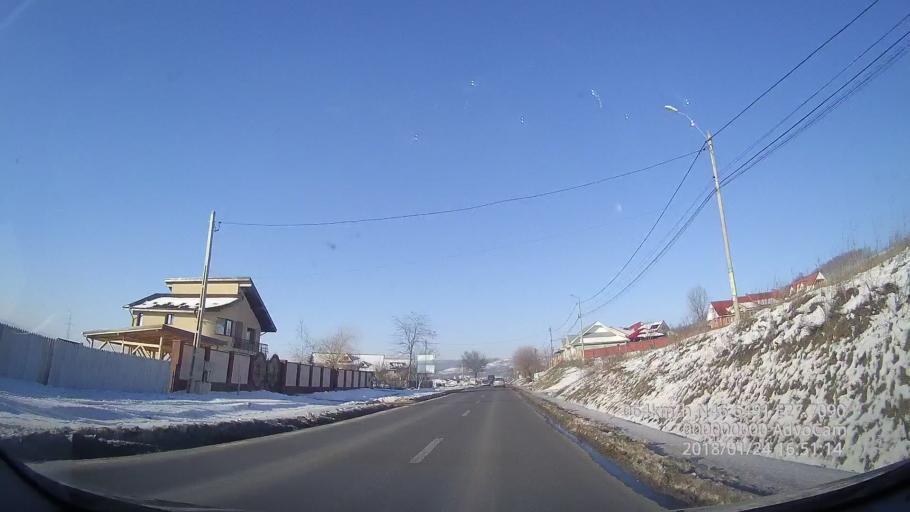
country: RO
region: Vaslui
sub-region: Municipiul Vaslui
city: Rediu
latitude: 46.6496
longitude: 27.7089
